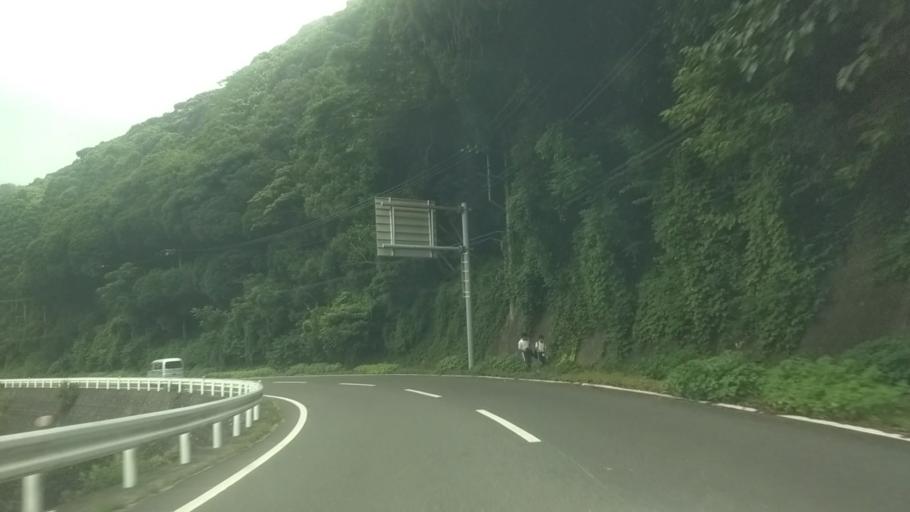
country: JP
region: Chiba
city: Kawaguchi
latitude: 35.1289
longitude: 140.1524
